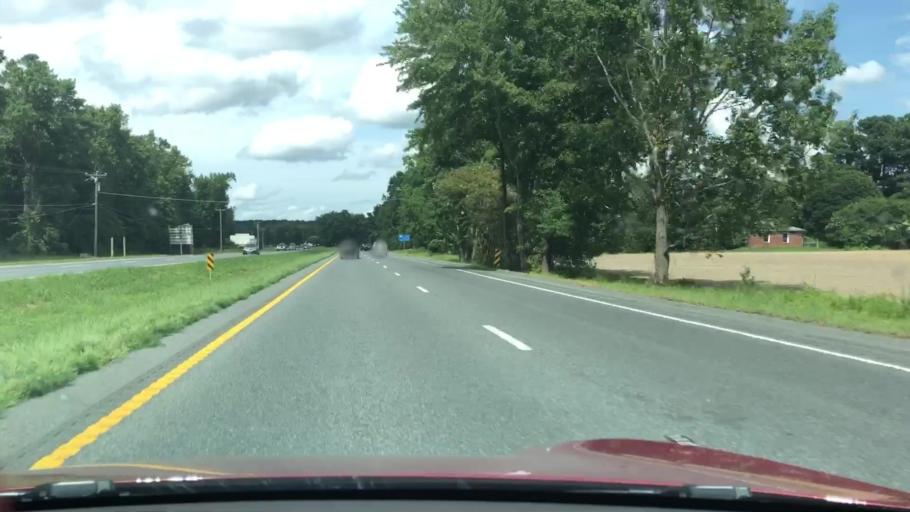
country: US
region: Virginia
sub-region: Accomack County
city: Wattsville
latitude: 37.9549
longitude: -75.5354
